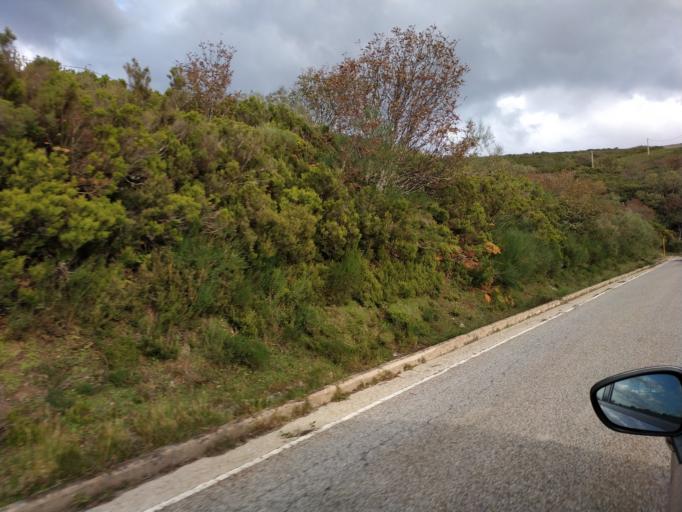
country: ES
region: Castille and Leon
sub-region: Provincia de Leon
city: Candin
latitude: 42.8703
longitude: -6.8208
